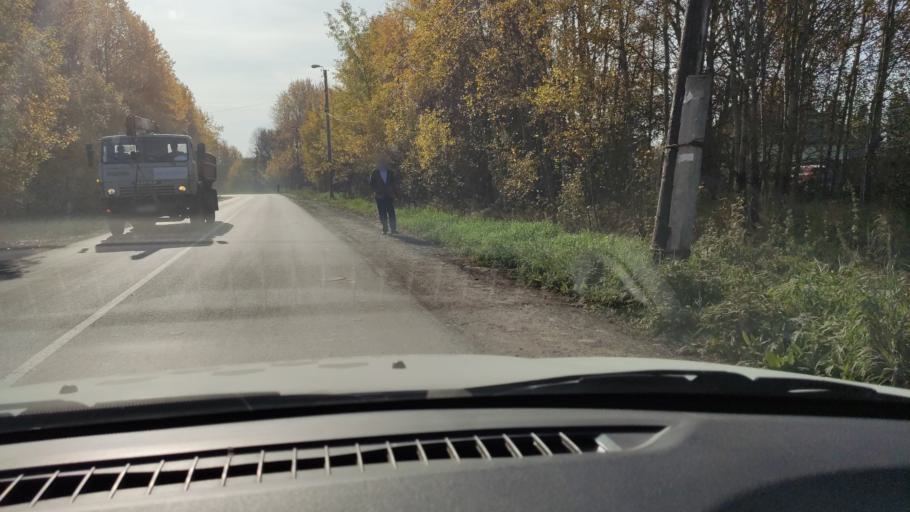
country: RU
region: Perm
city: Sylva
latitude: 58.0350
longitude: 56.7394
